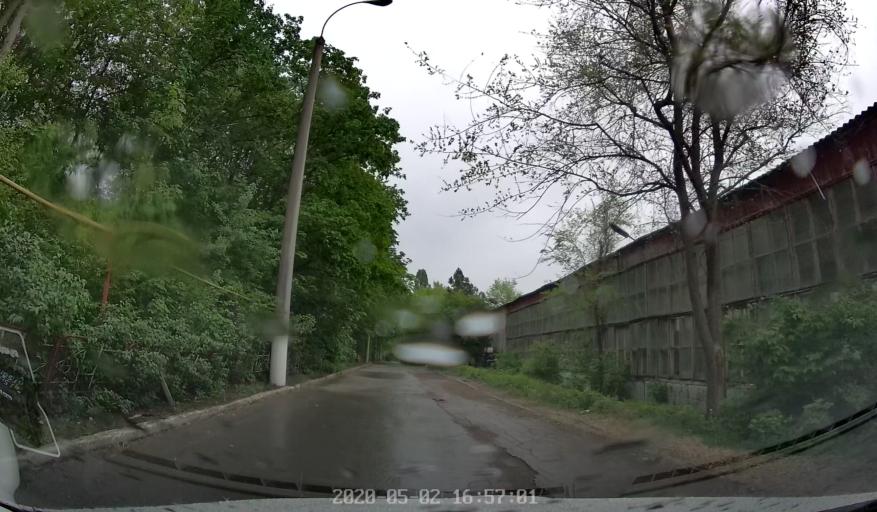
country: MD
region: Chisinau
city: Chisinau
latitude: 46.9753
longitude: 28.8322
